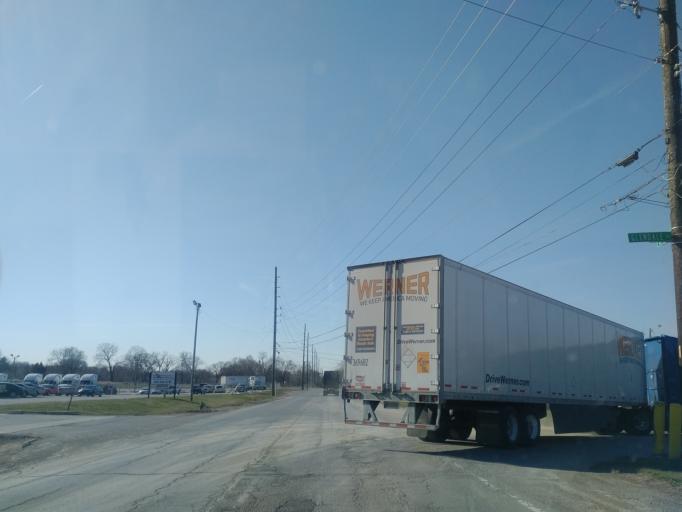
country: US
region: Indiana
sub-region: Marion County
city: Indianapolis
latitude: 39.7334
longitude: -86.1683
